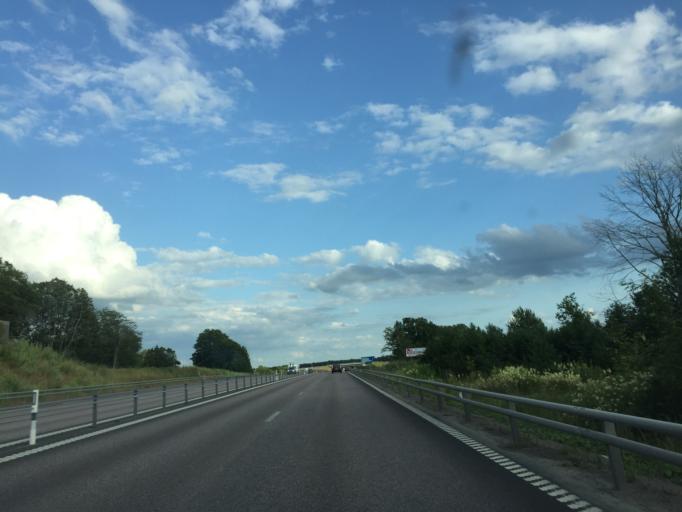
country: SE
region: OEstergoetland
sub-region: Motala Kommun
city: Motala
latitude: 58.5127
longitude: 15.0194
